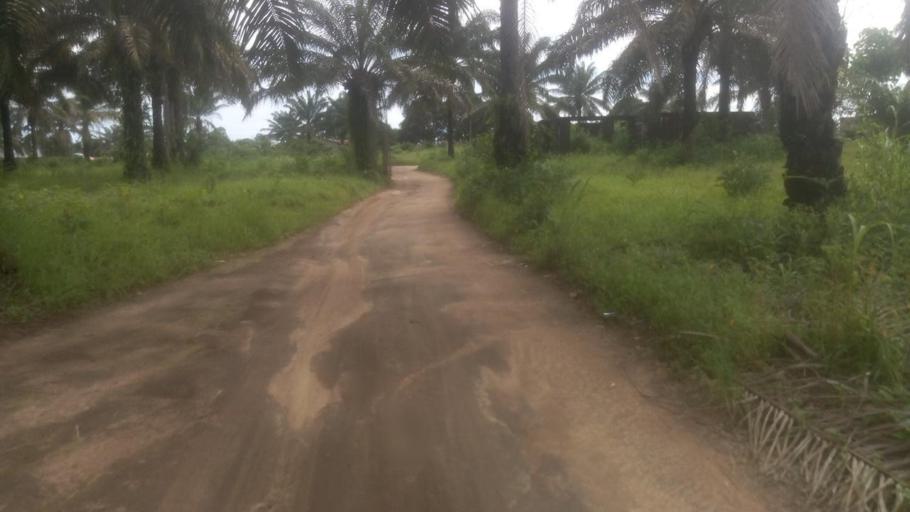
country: SL
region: Northern Province
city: Masoyila
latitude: 8.5959
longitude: -13.1882
